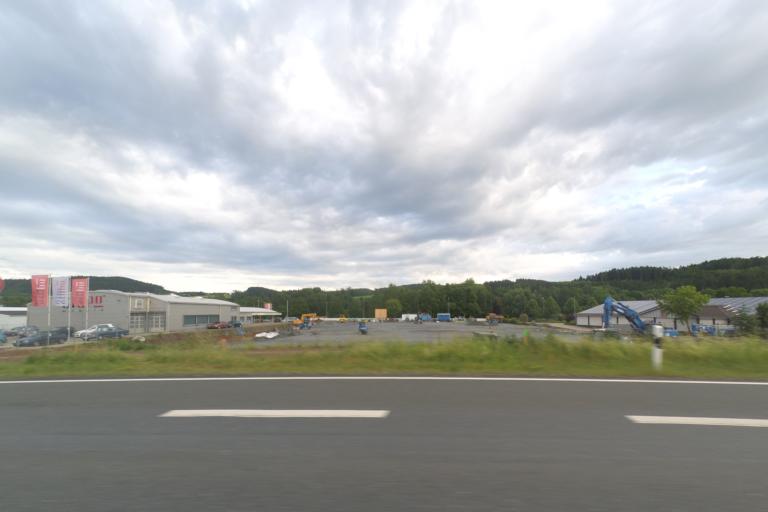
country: DE
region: Bavaria
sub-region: Upper Franconia
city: Kronach
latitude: 50.2331
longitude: 11.3509
